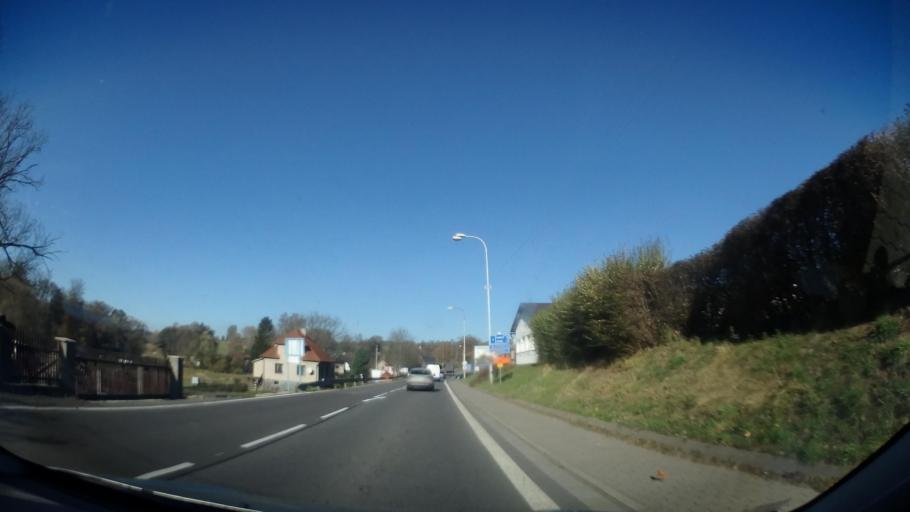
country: CZ
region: Pardubicky
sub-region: Okres Chrudim
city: Nasavrky
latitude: 49.7891
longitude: 15.8137
